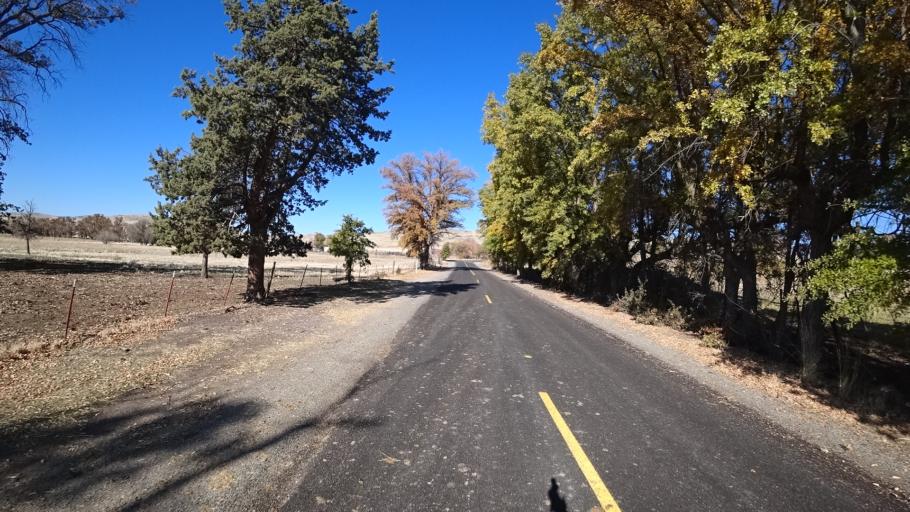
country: US
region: California
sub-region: Siskiyou County
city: Montague
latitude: 41.7250
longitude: -122.3891
